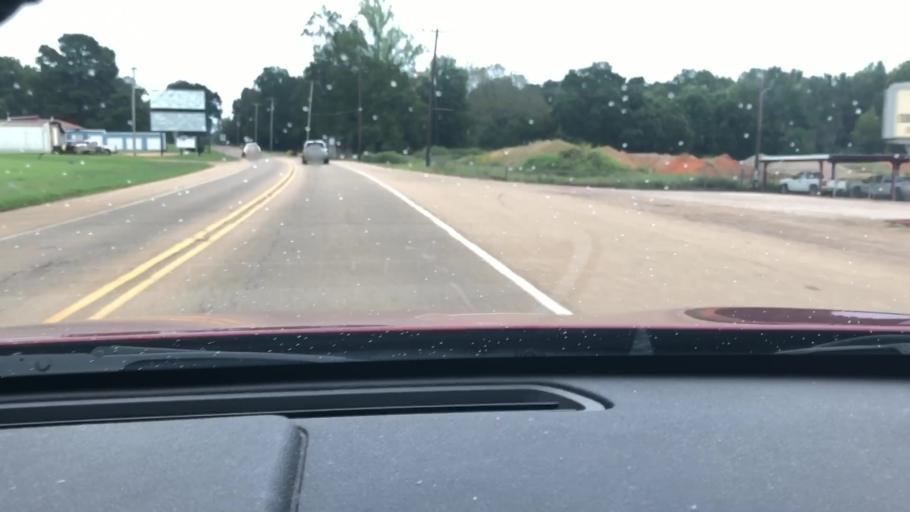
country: US
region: Arkansas
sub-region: Lafayette County
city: Stamps
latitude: 33.3661
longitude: -93.5096
